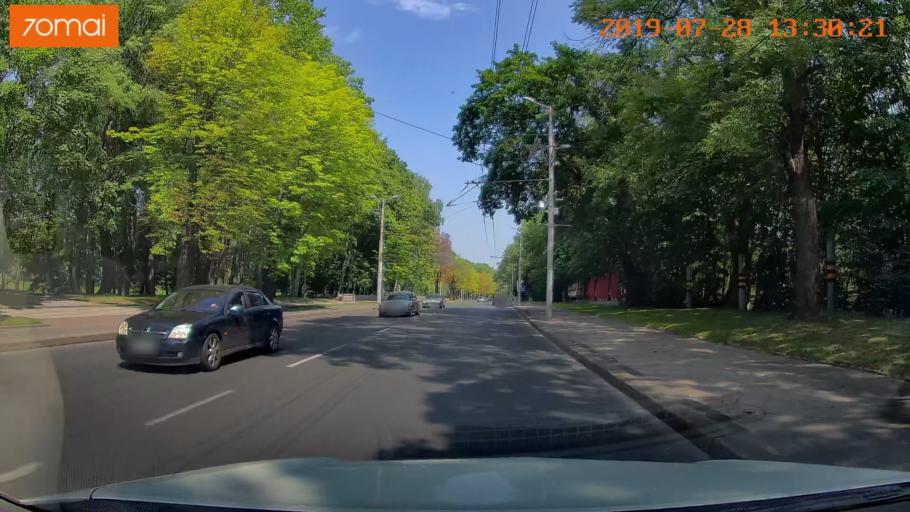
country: RU
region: Kaliningrad
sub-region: Gorod Kaliningrad
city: Kaliningrad
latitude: 54.7141
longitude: 20.4921
